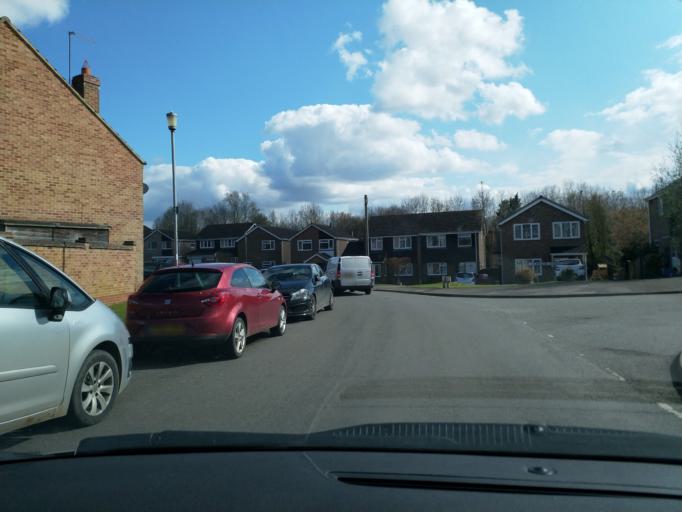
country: GB
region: England
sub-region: Oxfordshire
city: Adderbury
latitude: 52.0694
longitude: -1.2633
